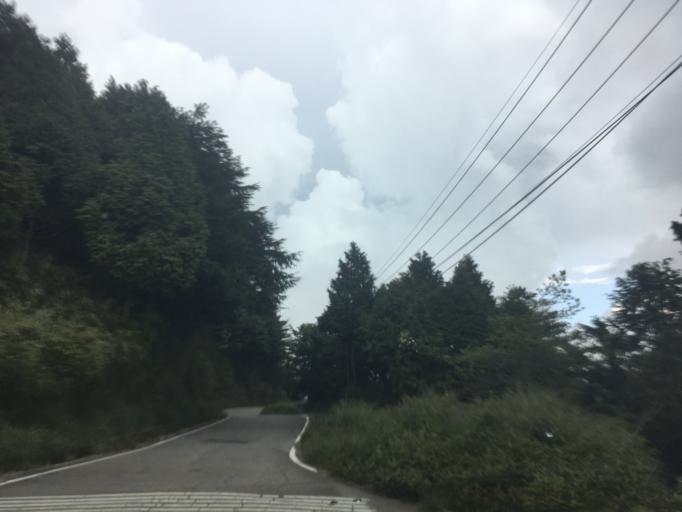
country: TW
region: Taiwan
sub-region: Nantou
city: Puli
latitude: 24.2691
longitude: 121.0306
